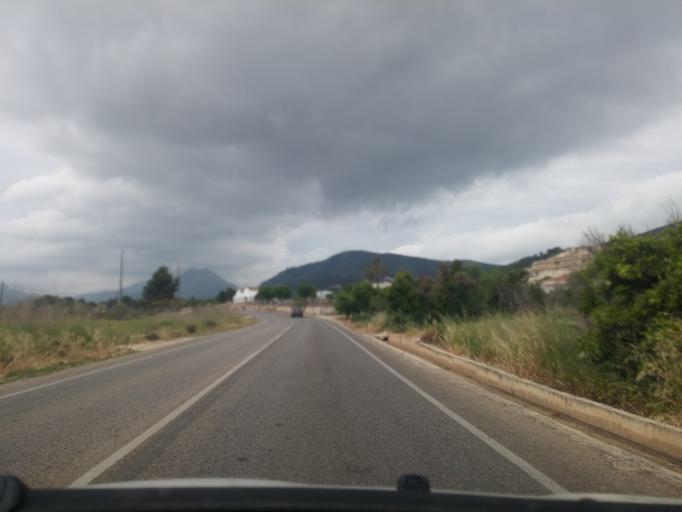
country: ES
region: Valencia
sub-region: Provincia de Alicante
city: Jalon
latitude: 38.7460
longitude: -0.0236
